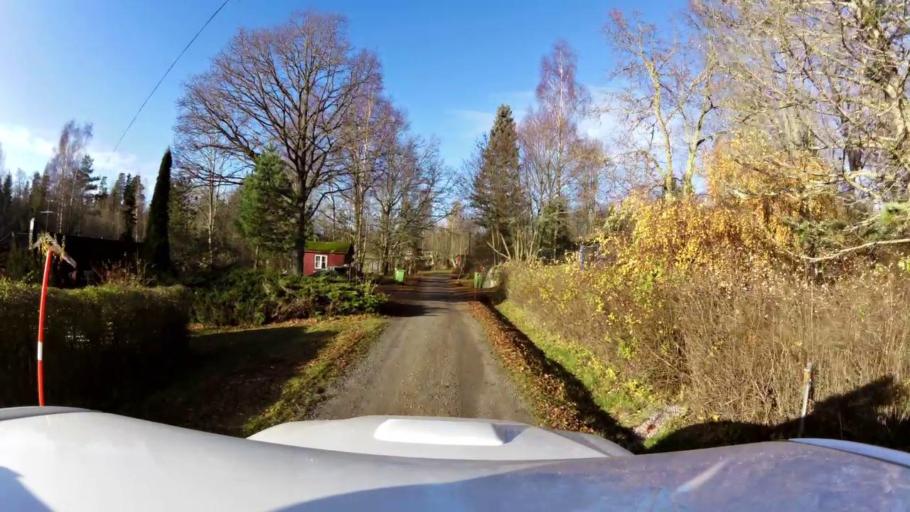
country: SE
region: OEstergoetland
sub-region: Linkopings Kommun
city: Sturefors
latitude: 58.2562
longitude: 15.7002
